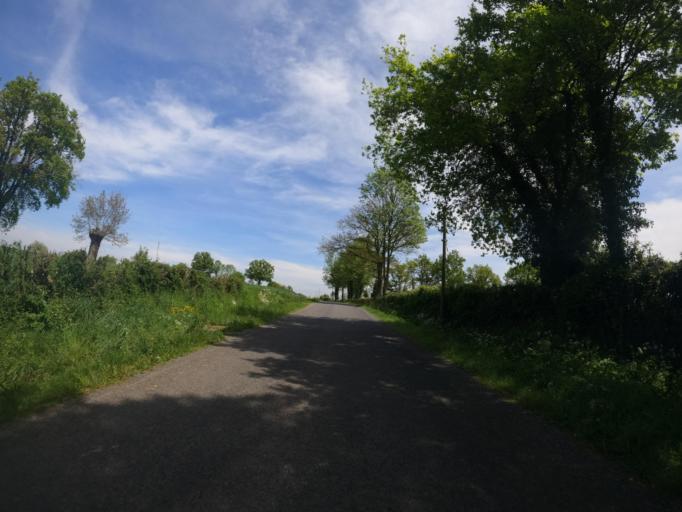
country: FR
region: Poitou-Charentes
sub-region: Departement des Deux-Sevres
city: Moncoutant
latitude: 46.6682
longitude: -0.5236
